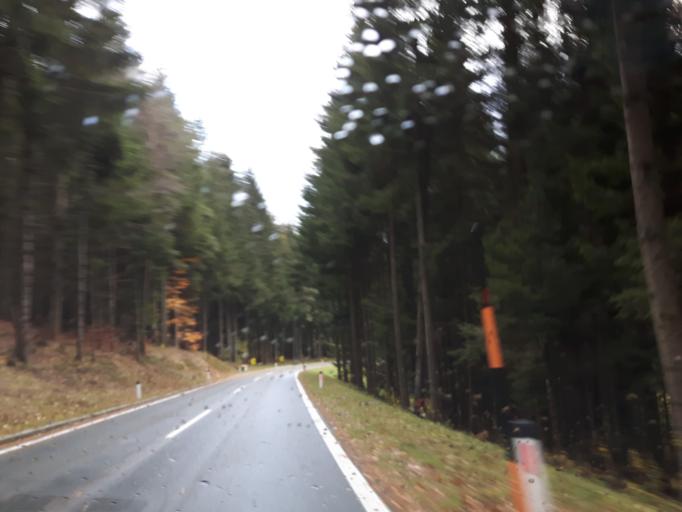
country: AT
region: Carinthia
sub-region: Politischer Bezirk Wolfsberg
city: Lavamund
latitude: 46.6532
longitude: 14.9803
